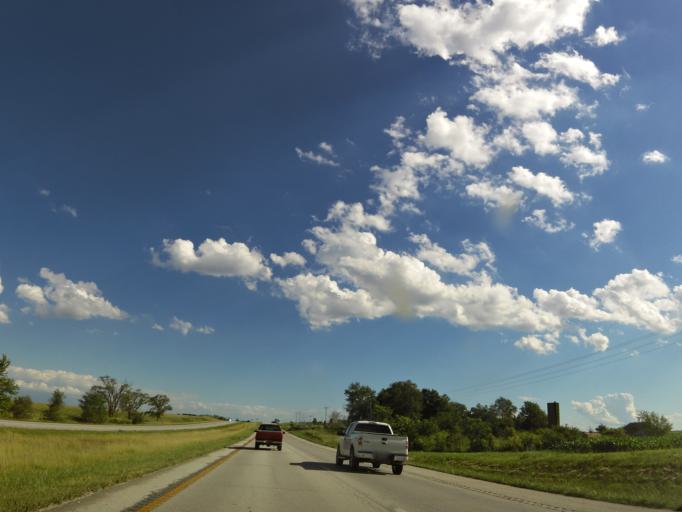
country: US
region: Missouri
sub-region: Marion County
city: Palmyra
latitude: 39.8709
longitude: -91.5254
